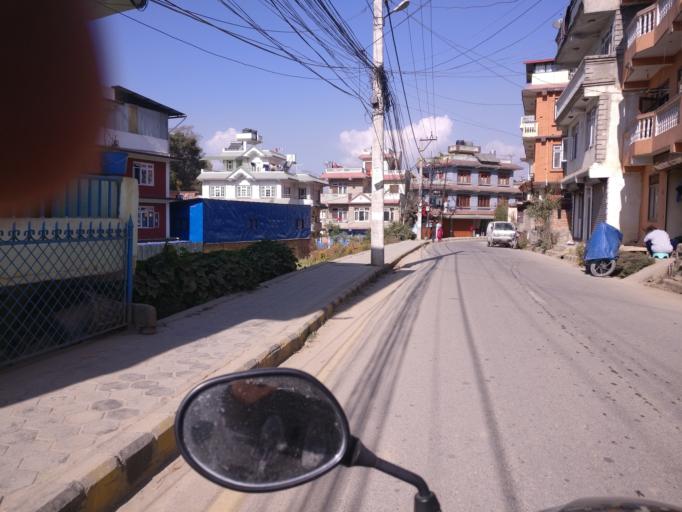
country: NP
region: Central Region
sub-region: Bagmati Zone
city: Patan
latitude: 27.6553
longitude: 85.3153
